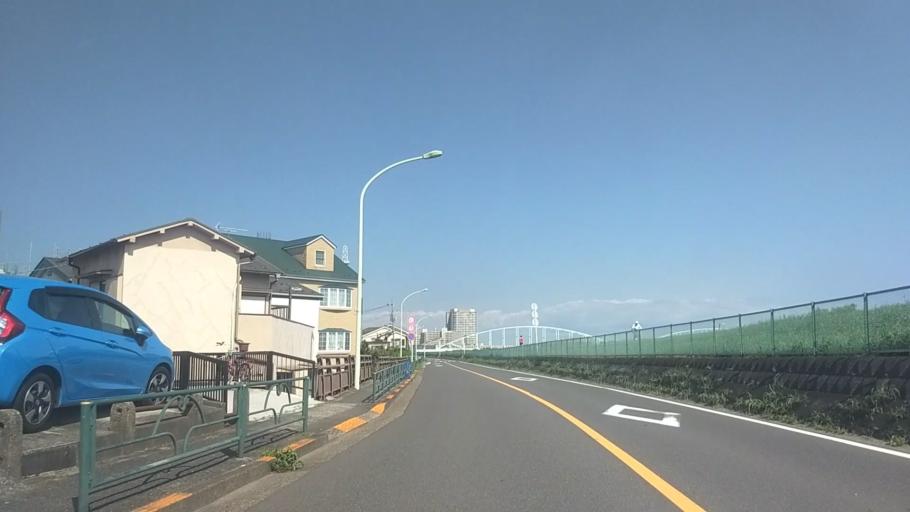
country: JP
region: Kanagawa
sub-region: Kawasaki-shi
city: Kawasaki
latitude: 35.5585
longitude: 139.6909
